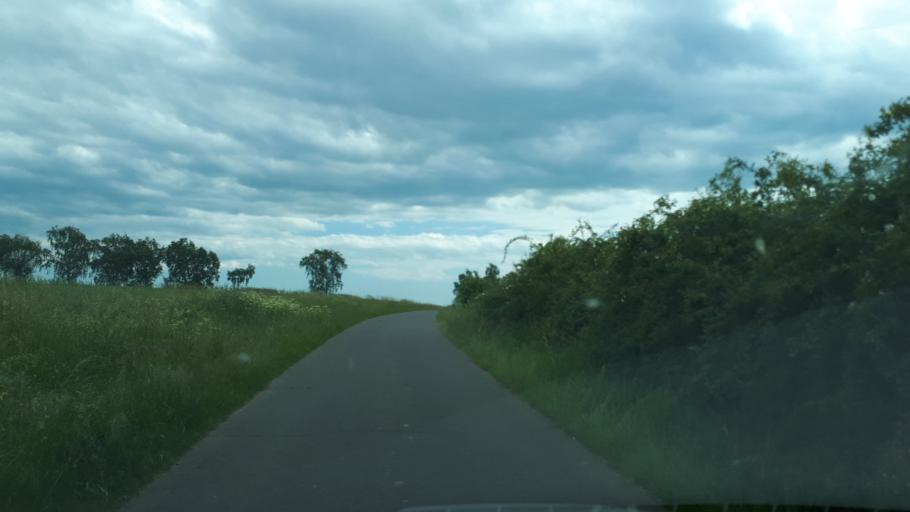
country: DE
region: Rheinland-Pfalz
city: Greimersburg
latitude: 50.1914
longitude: 7.1333
